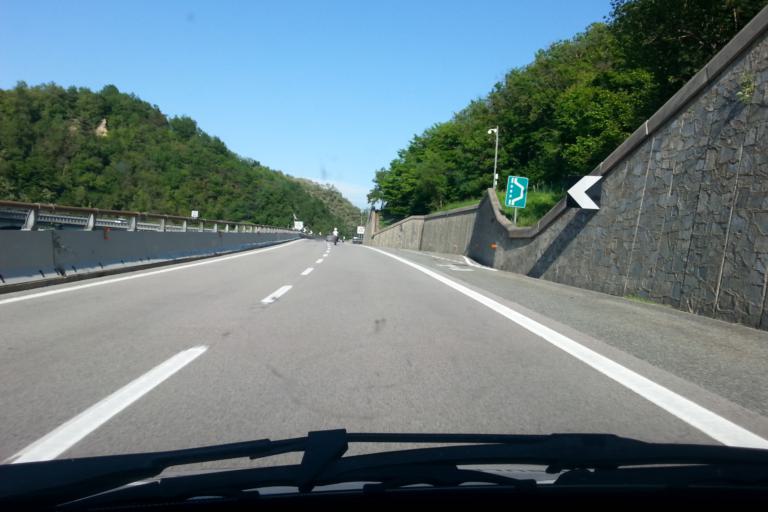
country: IT
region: Liguria
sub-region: Provincia di Savona
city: Valzemola
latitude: 44.3592
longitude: 8.1601
